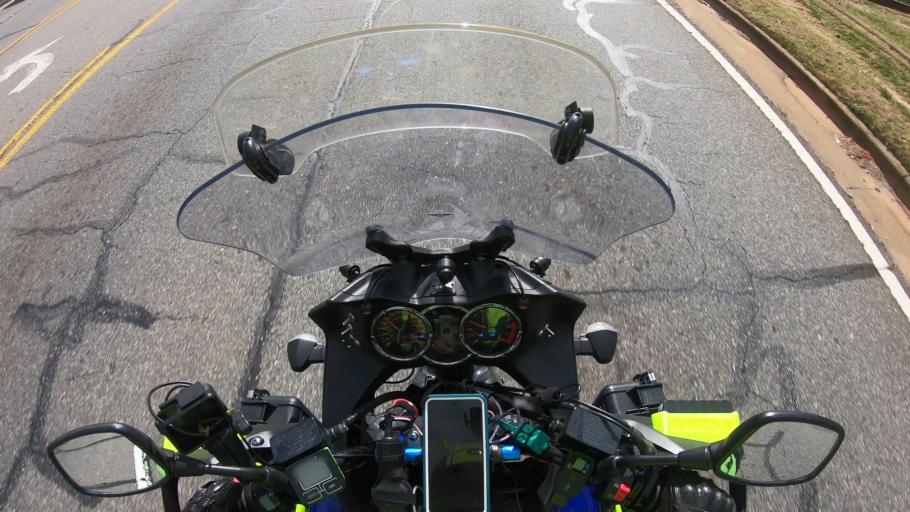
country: US
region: Georgia
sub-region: Cherokee County
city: Woodstock
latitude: 34.0681
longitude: -84.5225
